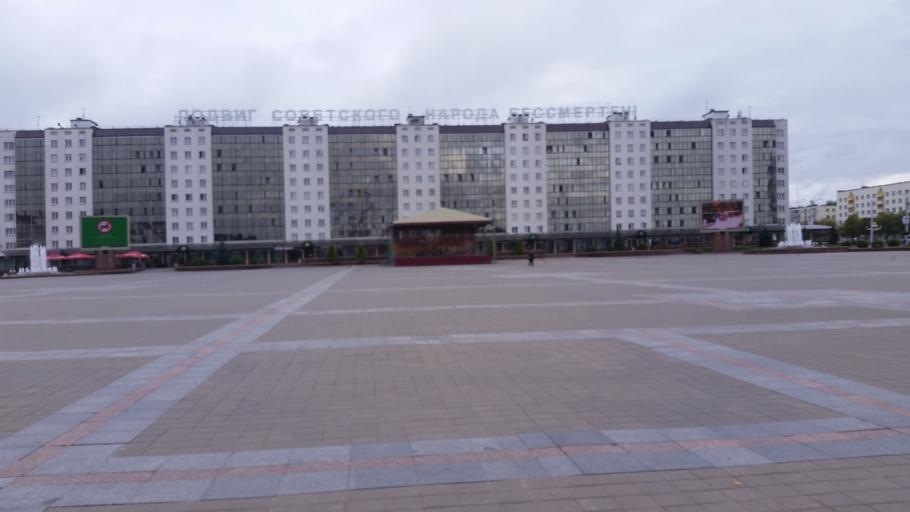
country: BY
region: Vitebsk
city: Vitebsk
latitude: 55.1841
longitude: 30.2037
